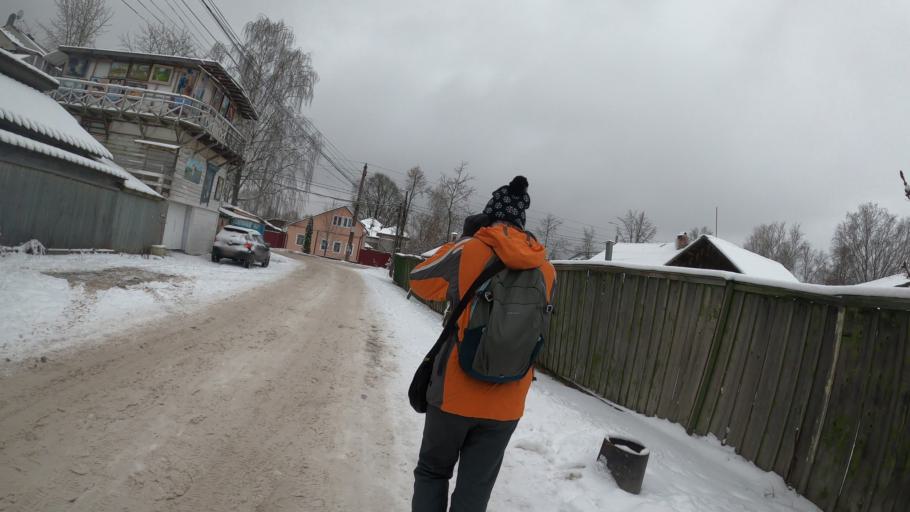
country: RU
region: Jaroslavl
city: Pereslavl'-Zalesskiy
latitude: 56.7386
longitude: 38.8415
